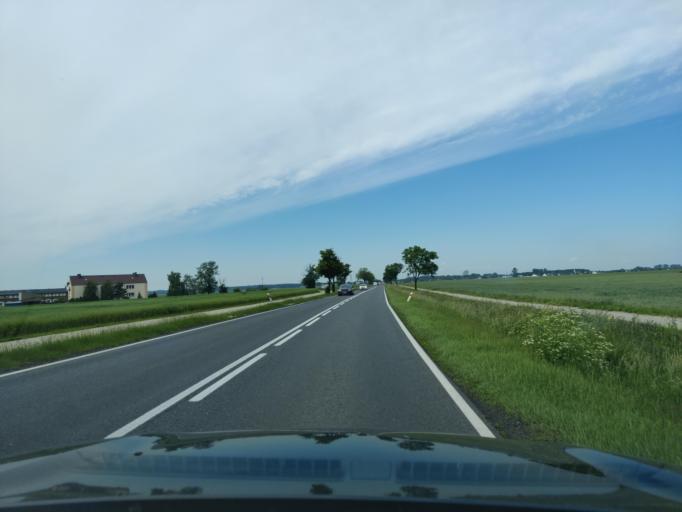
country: PL
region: Greater Poland Voivodeship
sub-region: Powiat poznanski
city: Steszew
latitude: 52.2546
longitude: 16.6415
